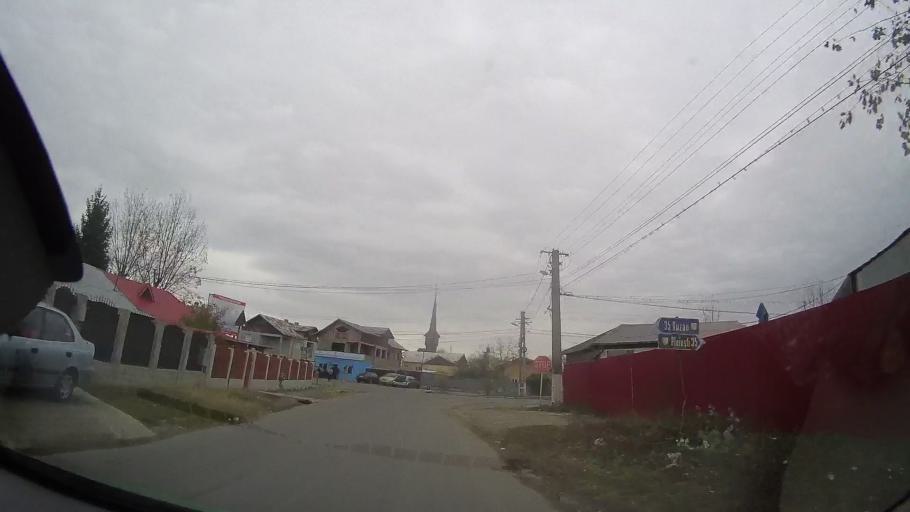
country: RO
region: Prahova
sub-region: Oras Mizil
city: Mizil
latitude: 45.0005
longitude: 26.4336
